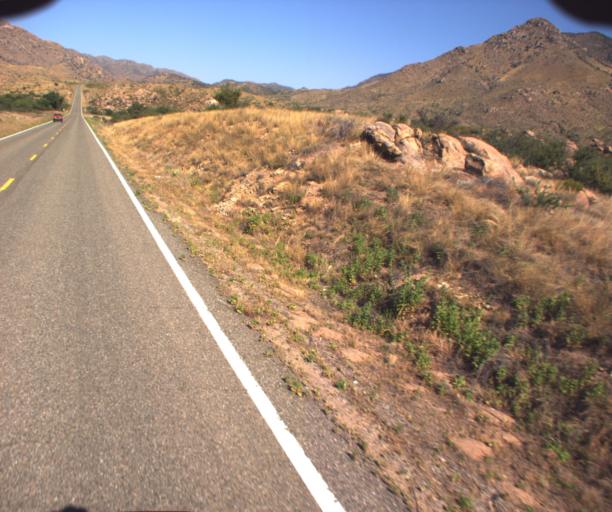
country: US
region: Arizona
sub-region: Graham County
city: Swift Trail Junction
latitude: 32.5602
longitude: -109.7555
